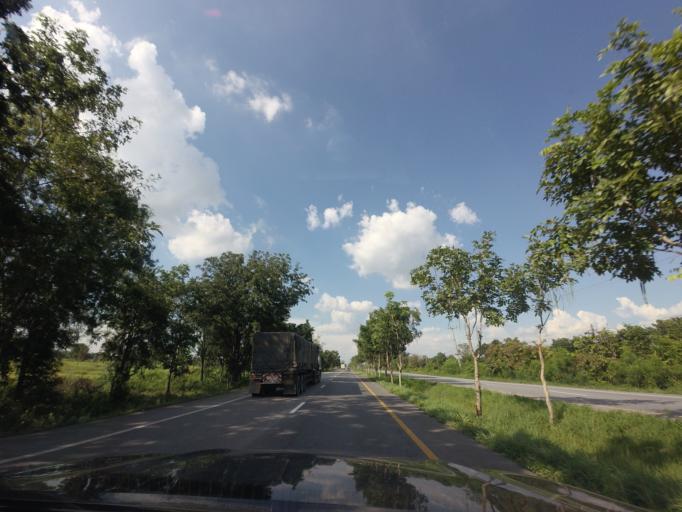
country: TH
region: Nakhon Ratchasima
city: Bua Lai
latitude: 15.7106
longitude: 102.5878
